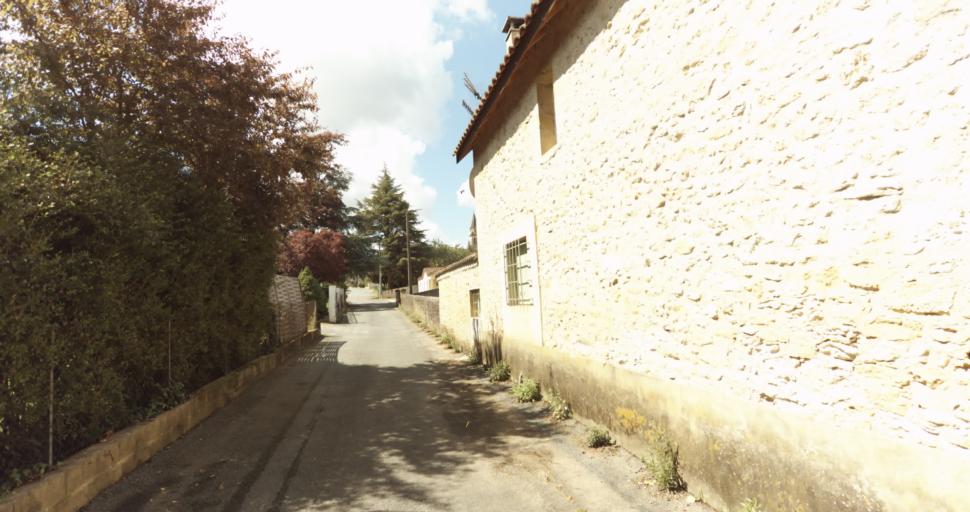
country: FR
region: Aquitaine
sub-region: Departement de la Dordogne
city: Le Bugue
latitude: 44.8451
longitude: 0.9102
